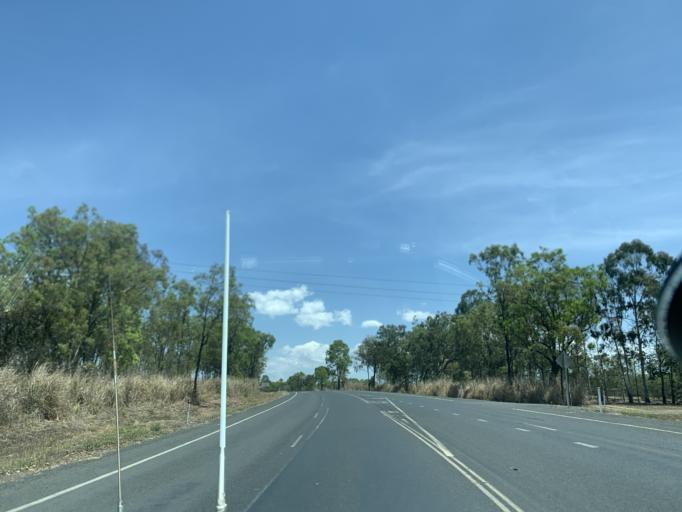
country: AU
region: Queensland
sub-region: Tablelands
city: Mareeba
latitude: -16.9687
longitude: 145.5347
